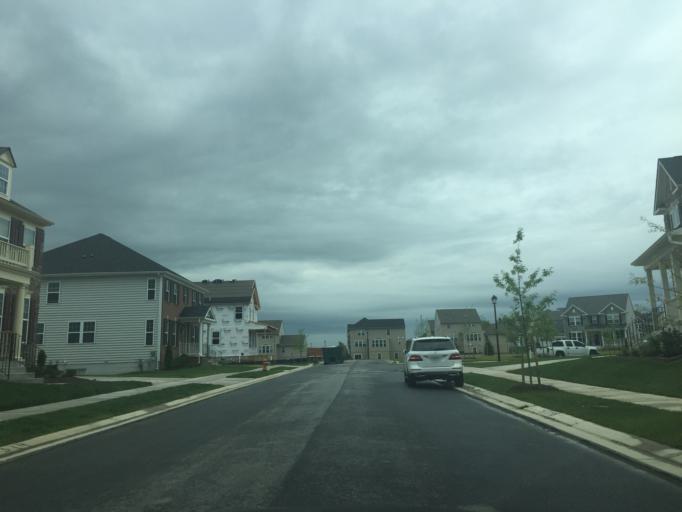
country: US
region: Maryland
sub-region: Baltimore County
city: Perry Hall
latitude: 39.4127
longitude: -76.4478
